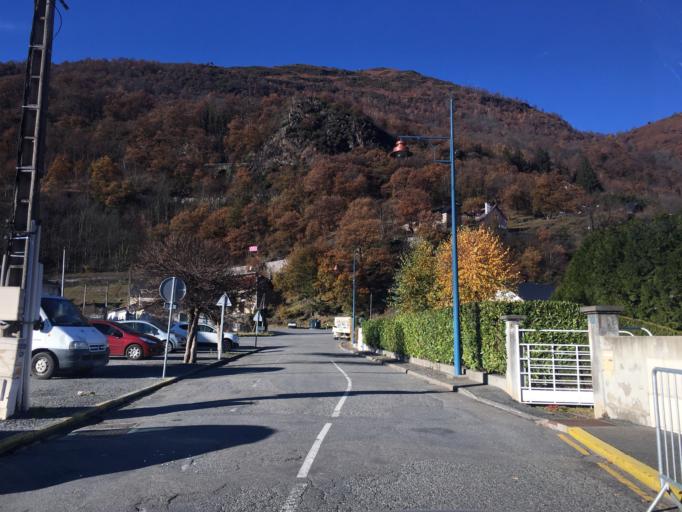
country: FR
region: Midi-Pyrenees
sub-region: Departement des Hautes-Pyrenees
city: Pierrefitte-Nestalas
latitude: 42.9593
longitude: -0.0759
